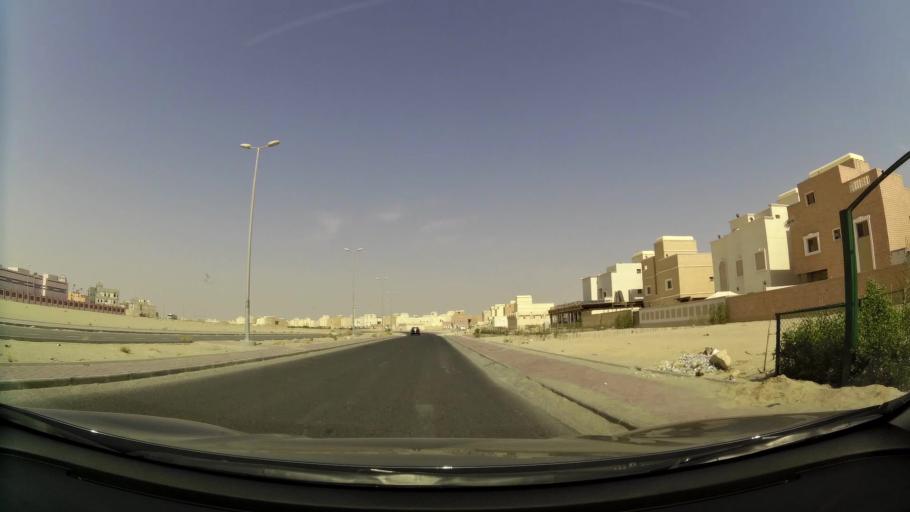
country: KW
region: Al Ahmadi
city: Al Wafrah
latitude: 28.7935
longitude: 48.0659
